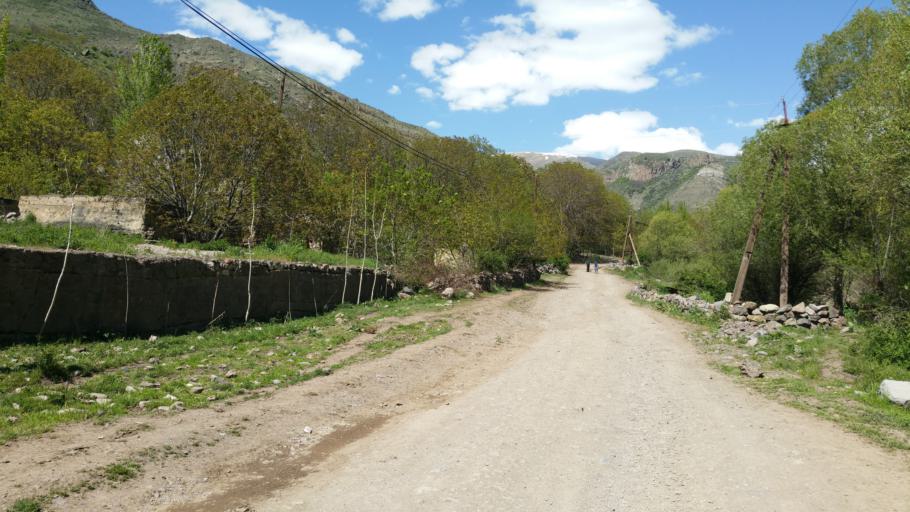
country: AM
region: Vayots' Dzori Marz
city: Yeghegis
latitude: 39.8733
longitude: 45.3307
